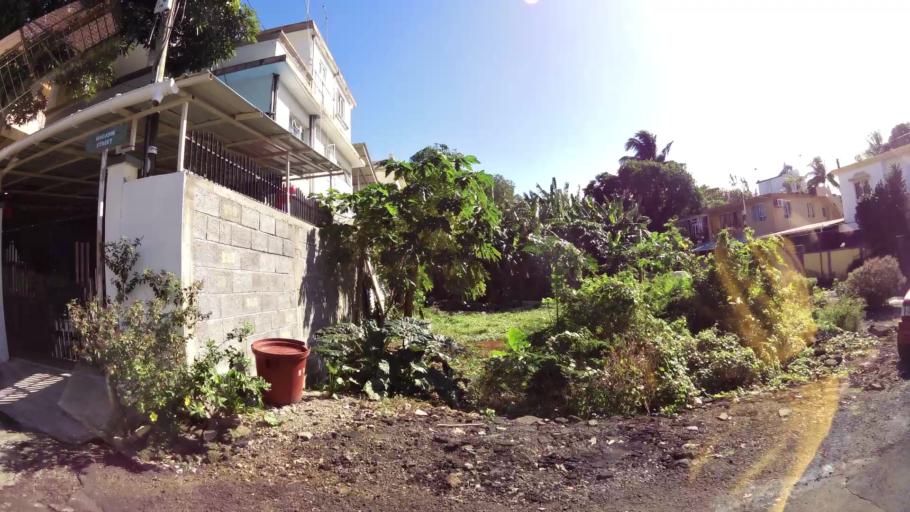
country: MU
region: Grand Port
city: Mahebourg
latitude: -20.4048
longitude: 57.7021
